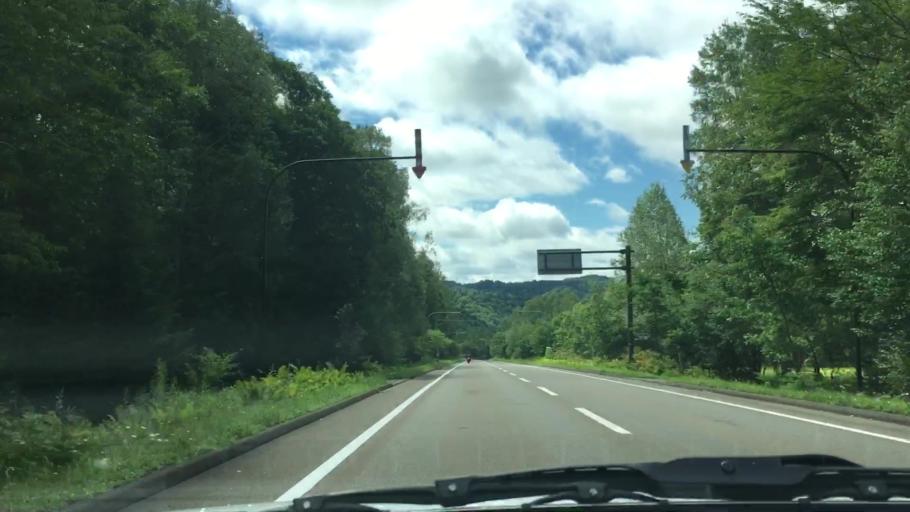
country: JP
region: Hokkaido
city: Kitami
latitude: 43.3962
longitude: 143.9246
